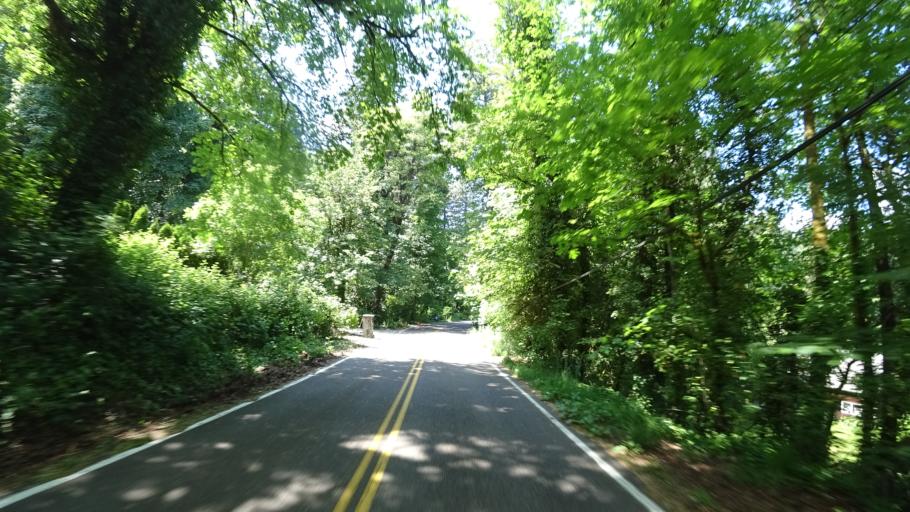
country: US
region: Oregon
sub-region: Clackamas County
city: Lake Oswego
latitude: 45.4444
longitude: -122.7001
